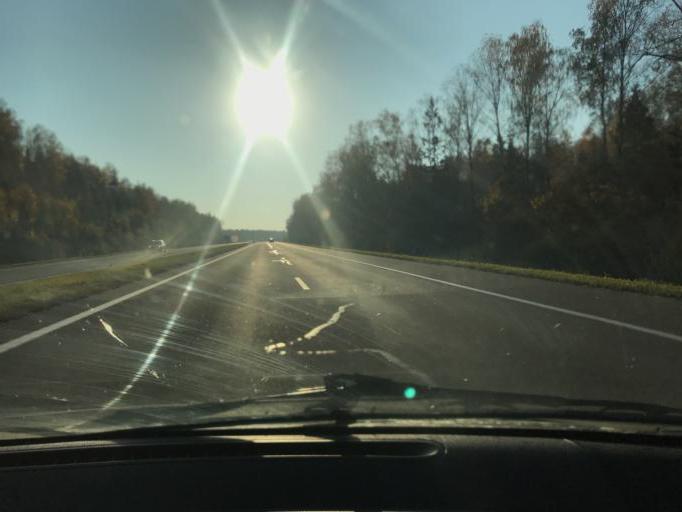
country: BY
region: Minsk
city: Loshnitsa
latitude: 54.2764
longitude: 28.7259
